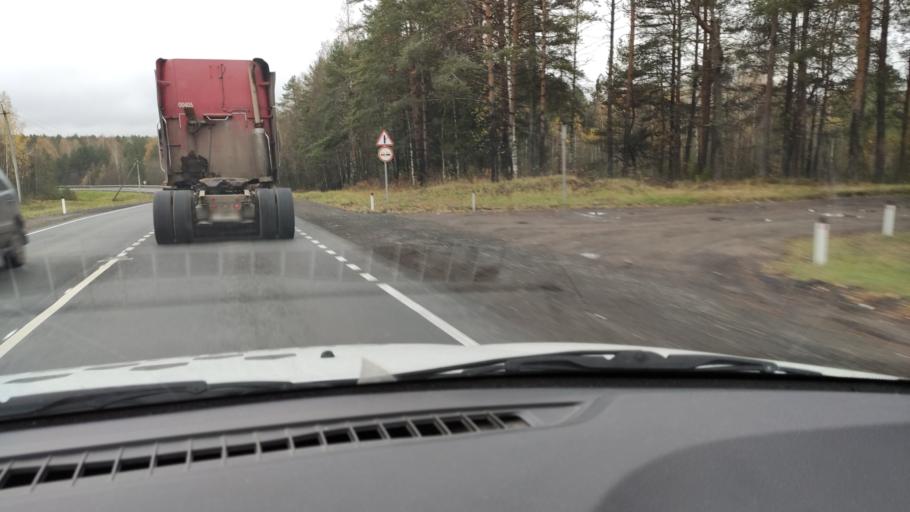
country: RU
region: Kirov
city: Belaya Kholunitsa
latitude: 58.8385
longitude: 50.6867
